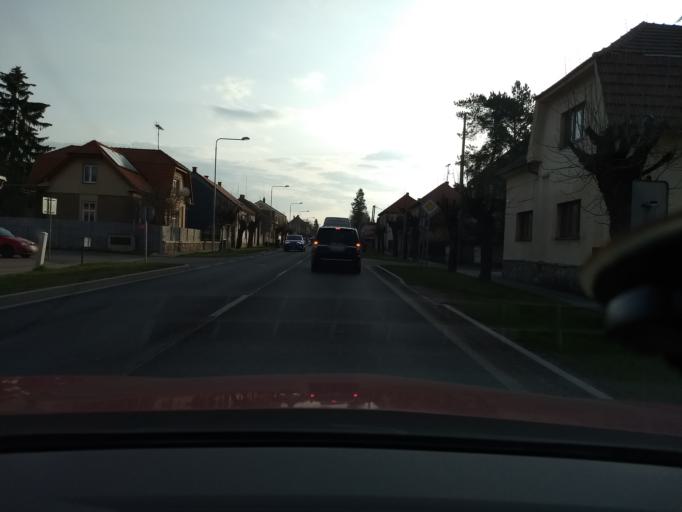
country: CZ
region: Central Bohemia
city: Rudna
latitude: 50.0358
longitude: 14.2368
